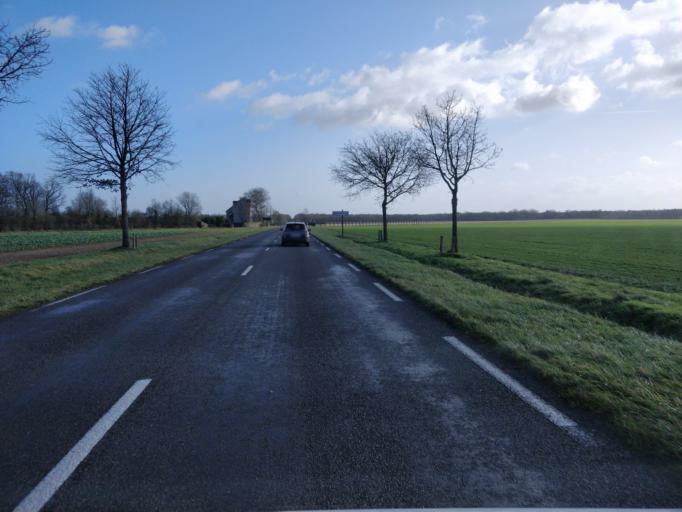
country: FR
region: Ile-de-France
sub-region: Departement de Seine-et-Marne
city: Bagneaux-sur-Loing
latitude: 48.2526
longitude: 2.7593
